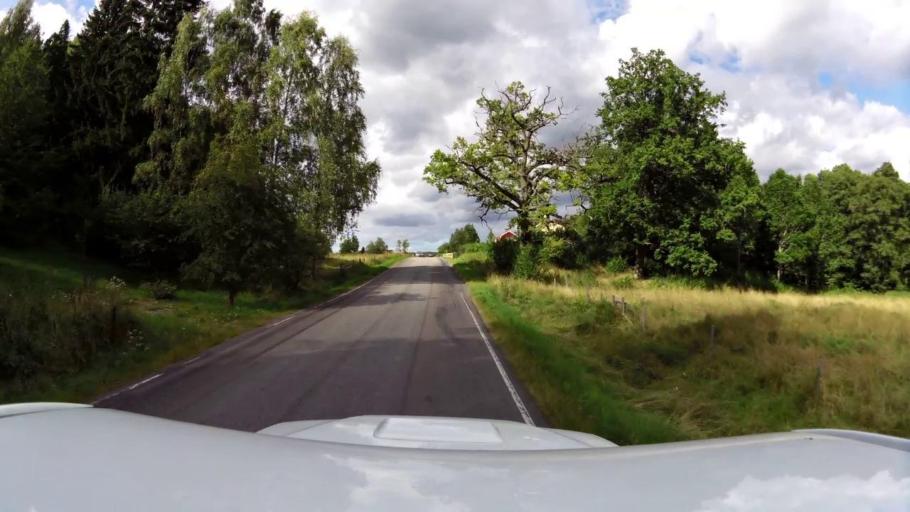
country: SE
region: OEstergoetland
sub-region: Linkopings Kommun
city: Sturefors
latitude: 58.3242
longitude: 15.7165
